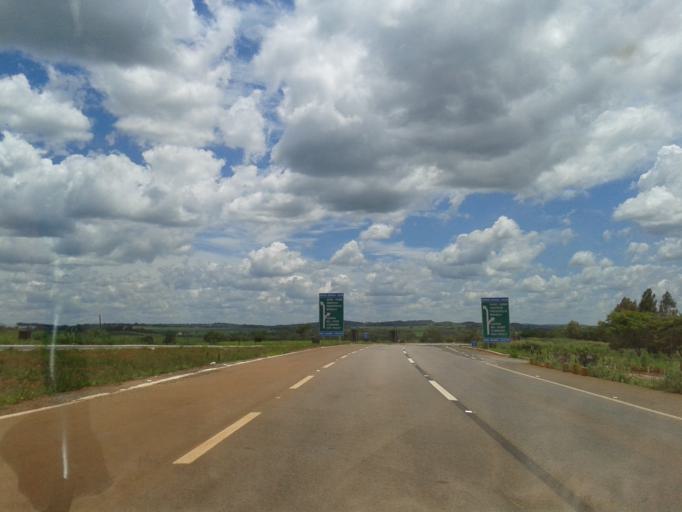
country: BR
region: Goias
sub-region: Neropolis
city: Neropolis
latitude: -16.3773
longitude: -49.2242
